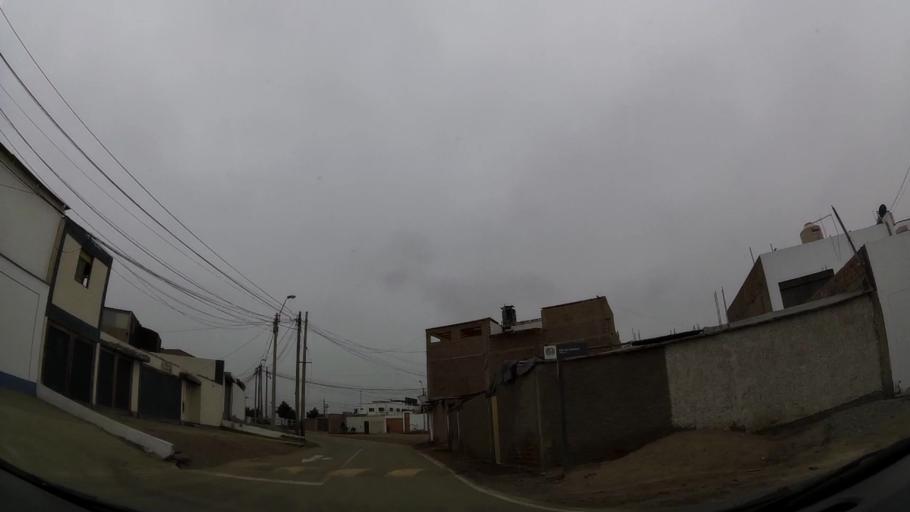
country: PE
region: Lima
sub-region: Lima
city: Punta Hermosa
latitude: -12.3180
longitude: -76.8335
